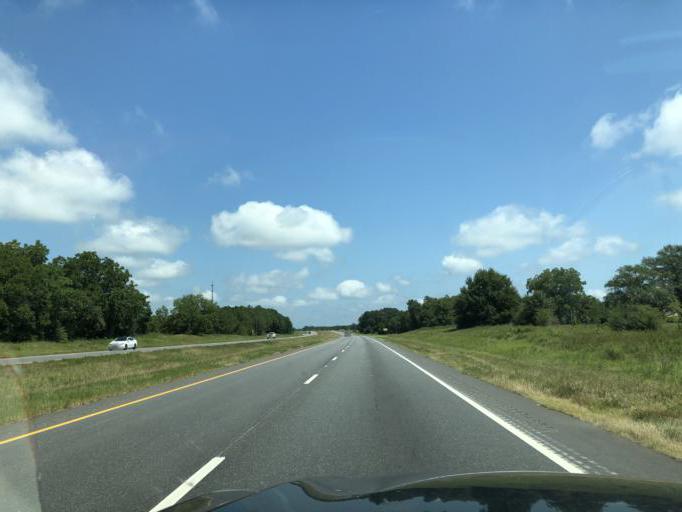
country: US
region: Alabama
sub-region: Henry County
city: Abbeville
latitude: 31.4989
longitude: -85.2934
